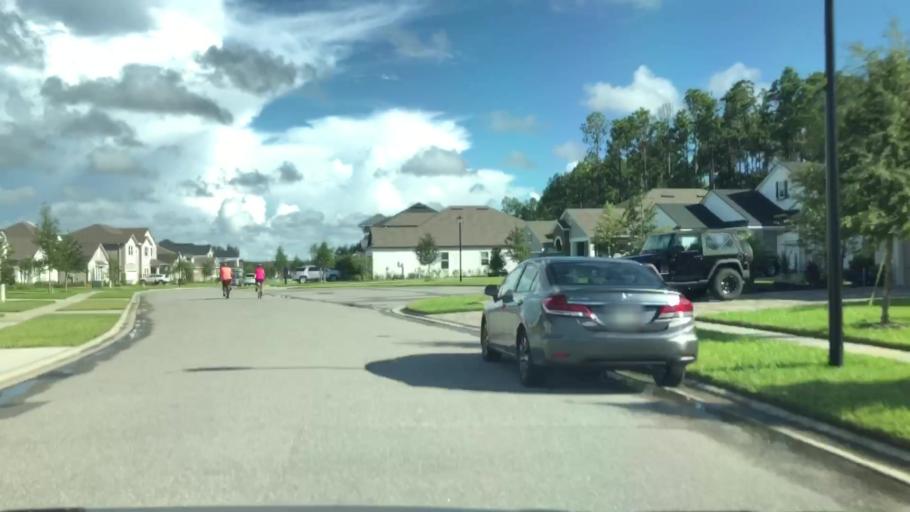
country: US
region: Florida
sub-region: Saint Johns County
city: Palm Valley
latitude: 30.1312
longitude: -81.4085
